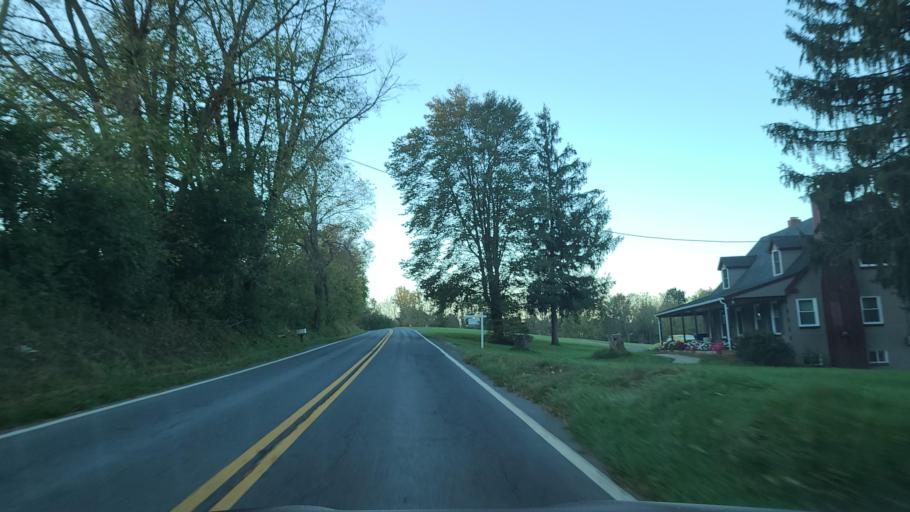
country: US
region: Maryland
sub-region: Frederick County
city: Jefferson
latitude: 39.3846
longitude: -77.5384
